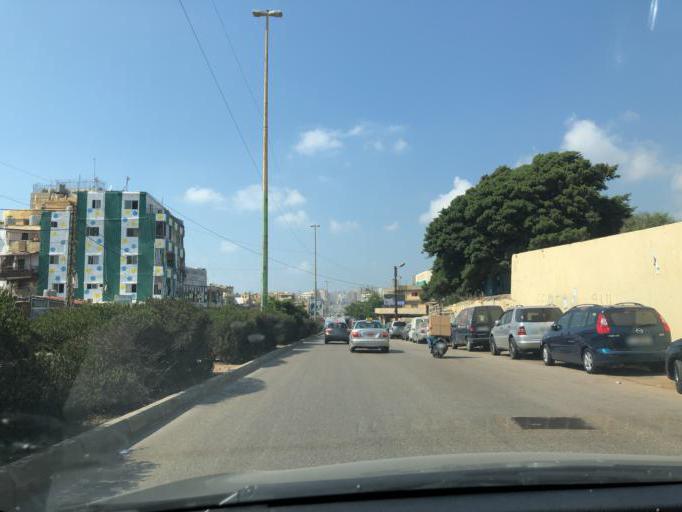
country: LB
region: Beyrouth
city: Beirut
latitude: 33.8506
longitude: 35.4852
